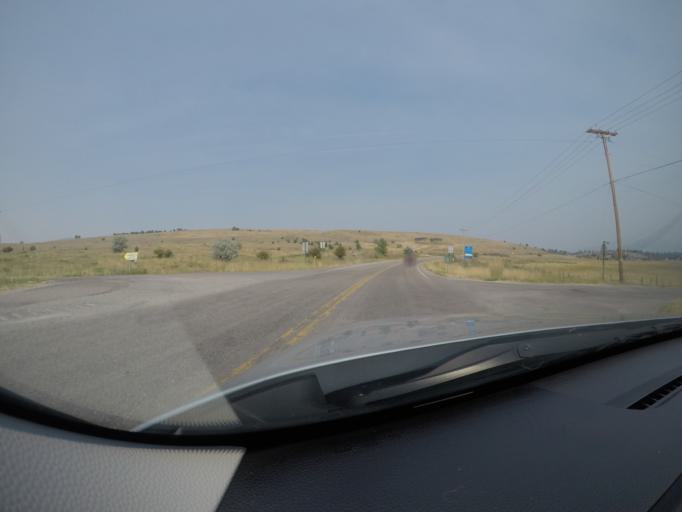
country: US
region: Montana
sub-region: Lake County
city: Polson
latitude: 47.7328
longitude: -114.1886
